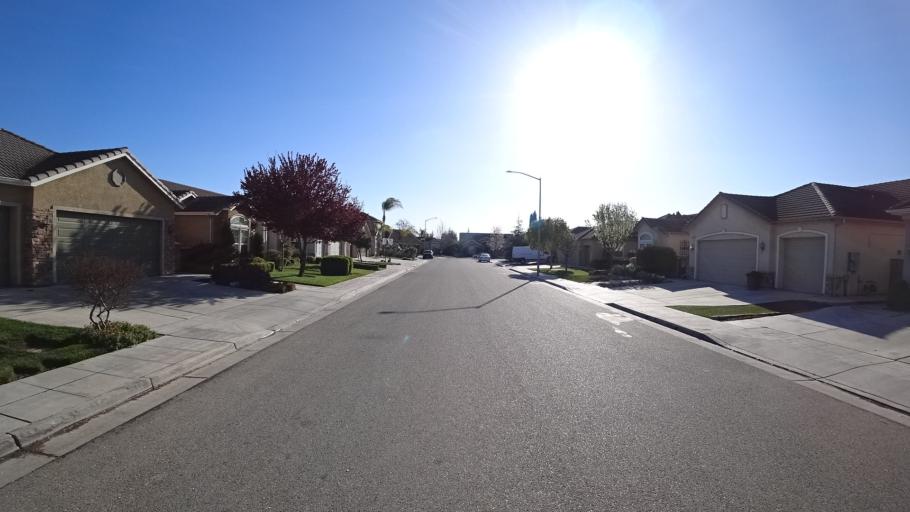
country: US
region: California
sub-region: Fresno County
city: Biola
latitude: 36.8323
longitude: -119.9011
